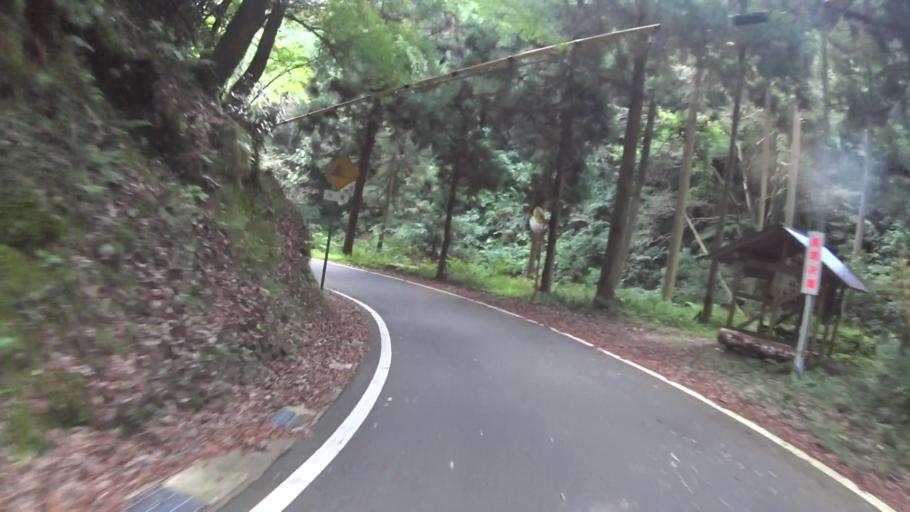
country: JP
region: Kyoto
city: Miyazu
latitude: 35.6105
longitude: 135.2063
